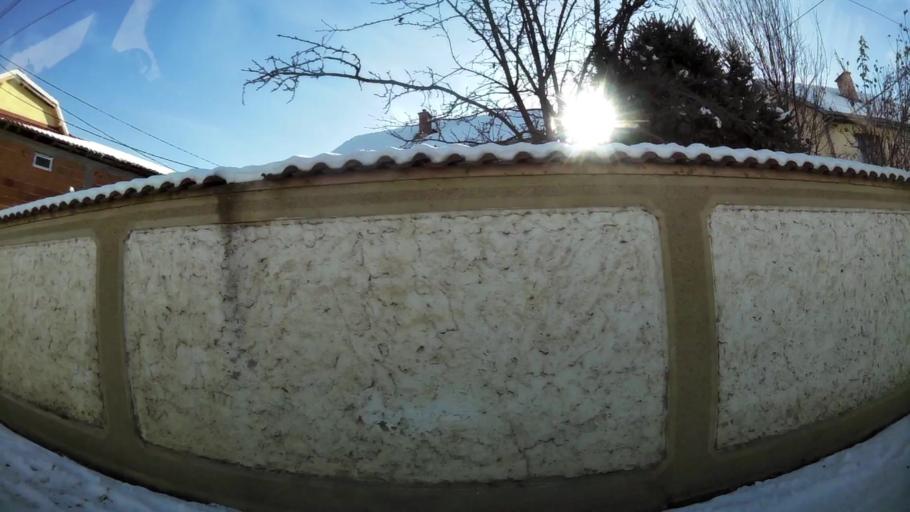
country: MK
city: Grchec
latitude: 41.9870
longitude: 21.3300
